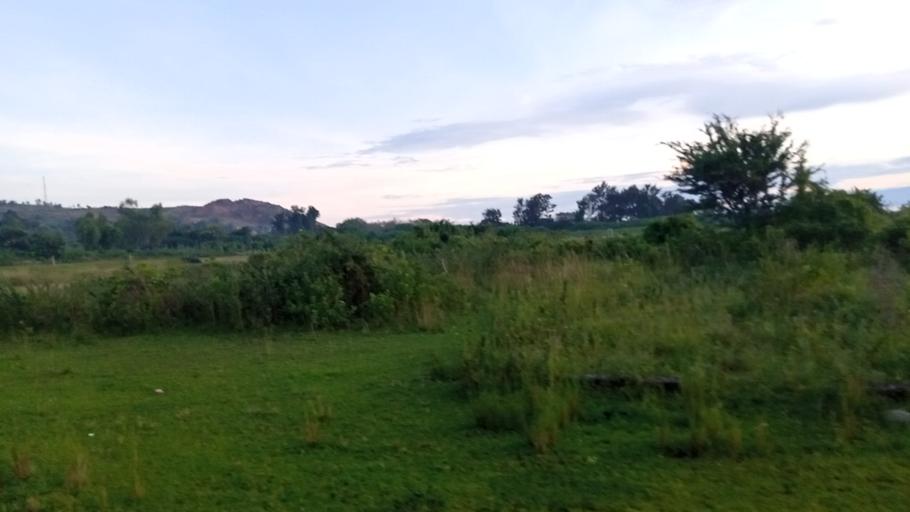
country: BI
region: Bujumbura Mairie
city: Bujumbura
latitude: -3.4897
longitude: 29.3480
